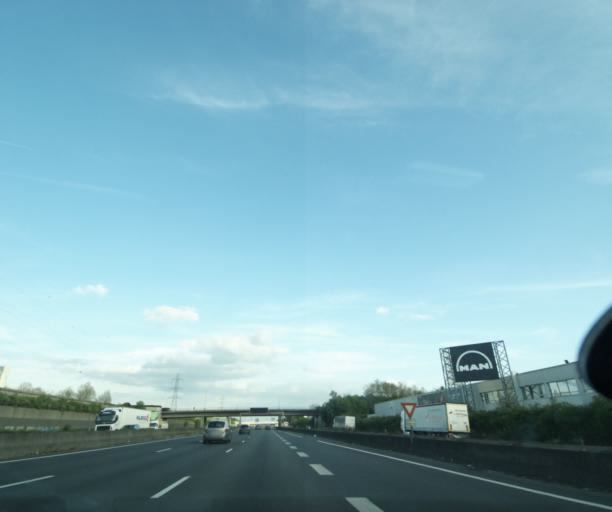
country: FR
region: Ile-de-France
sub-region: Departement de l'Essonne
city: Courcouronnes
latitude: 48.6306
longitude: 2.4087
